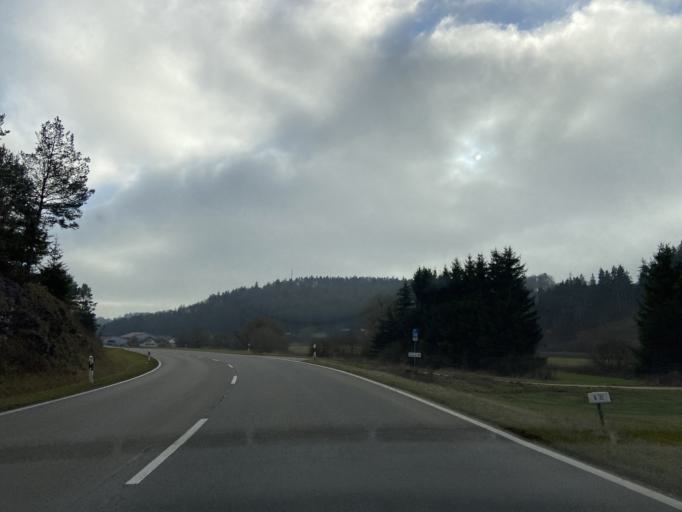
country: DE
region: Baden-Wuerttemberg
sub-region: Tuebingen Region
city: Neufra
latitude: 48.2578
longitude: 9.1740
